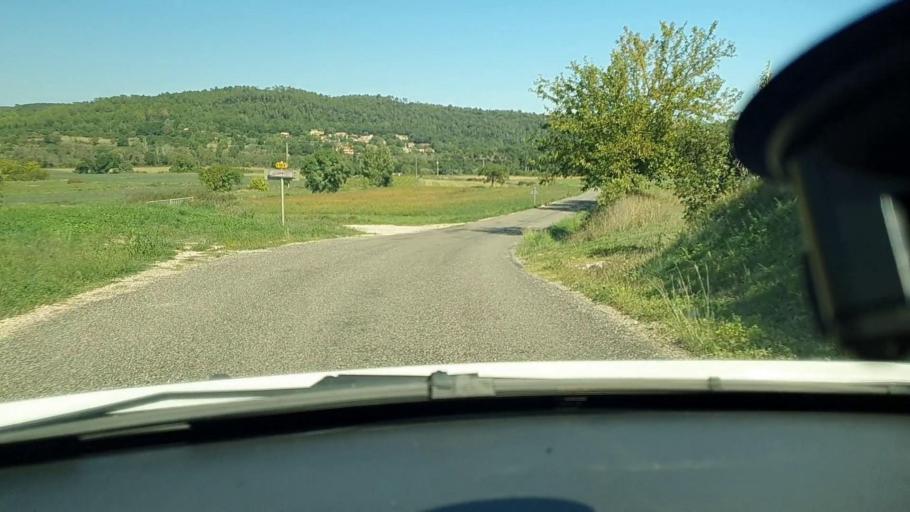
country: FR
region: Languedoc-Roussillon
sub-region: Departement du Gard
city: Goudargues
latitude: 44.1723
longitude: 4.4465
